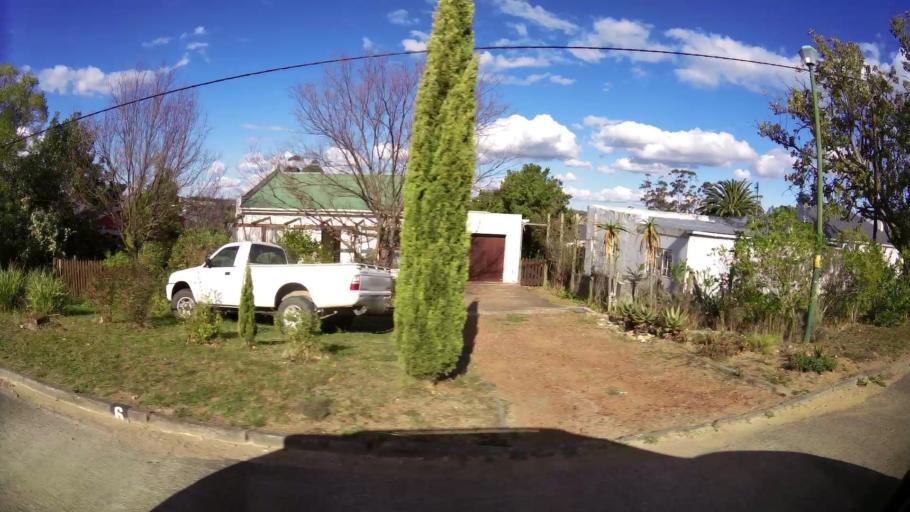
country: ZA
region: Western Cape
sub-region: Overberg District Municipality
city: Swellendam
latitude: -34.0182
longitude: 20.4378
